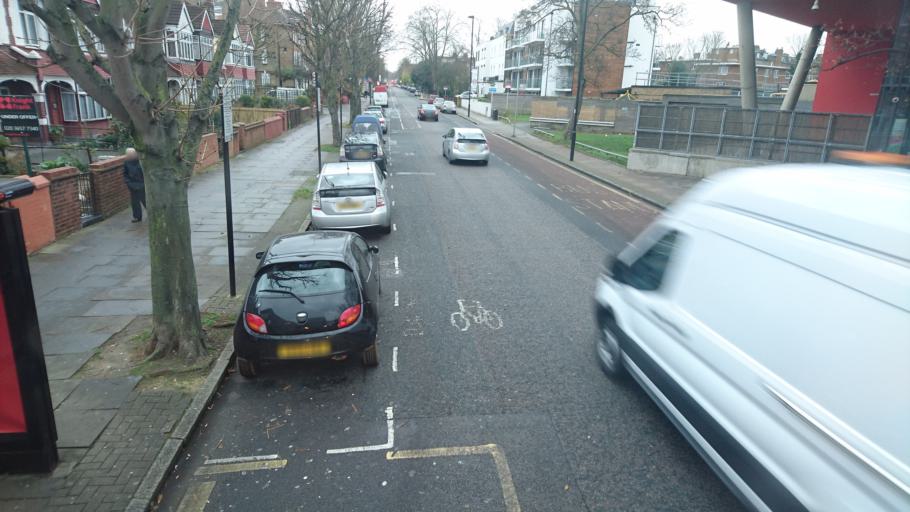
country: GB
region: England
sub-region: Greater London
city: Holloway
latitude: 51.5553
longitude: -0.1179
